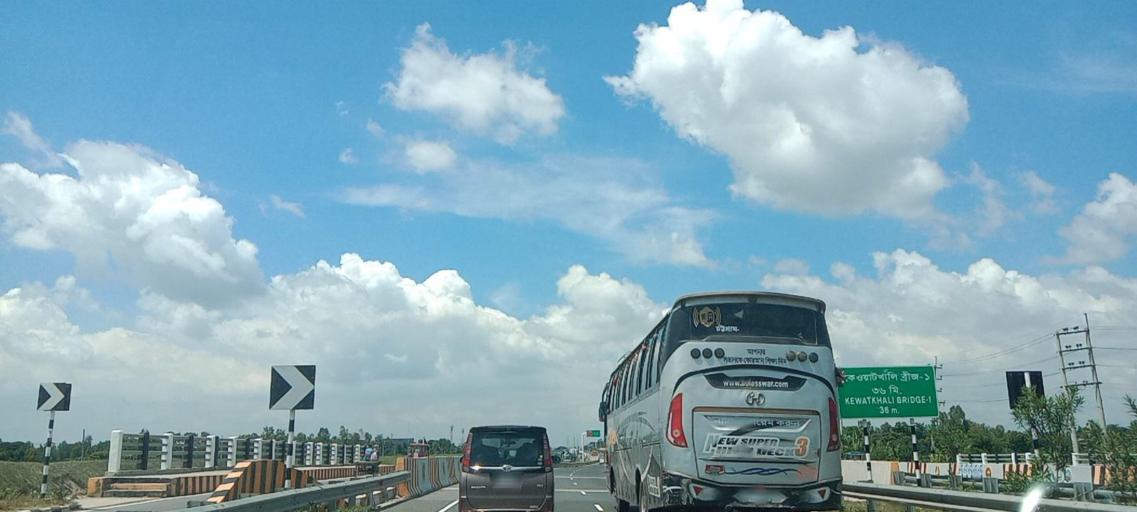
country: BD
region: Dhaka
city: Dohar
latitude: 23.5800
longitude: 90.3055
